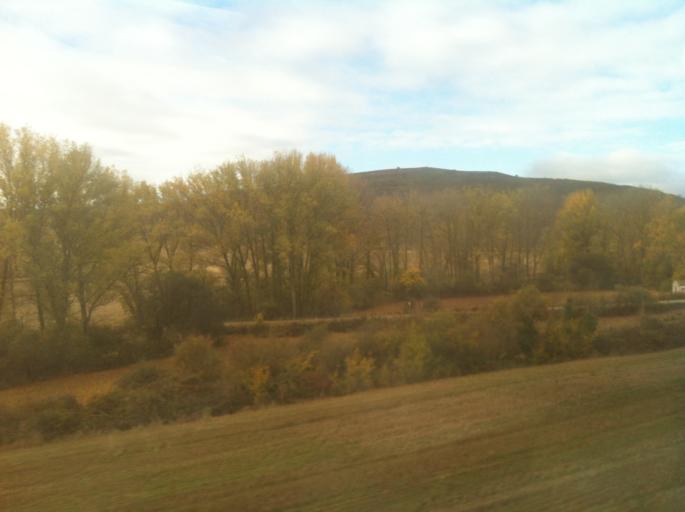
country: ES
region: Castille and Leon
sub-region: Provincia de Burgos
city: Santa Maria del Invierno
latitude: 42.4340
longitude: -3.4351
